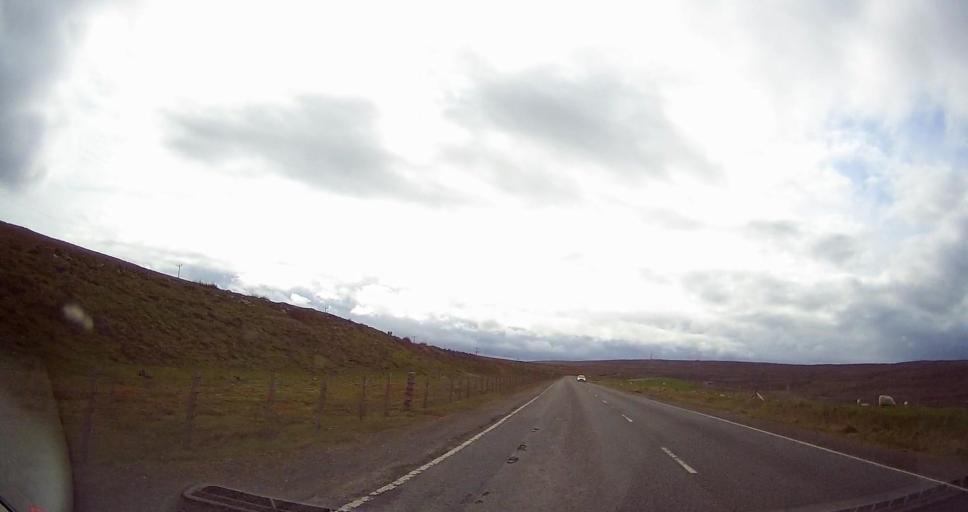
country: GB
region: Scotland
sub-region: Shetland Islands
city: Lerwick
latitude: 60.4453
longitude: -1.2467
